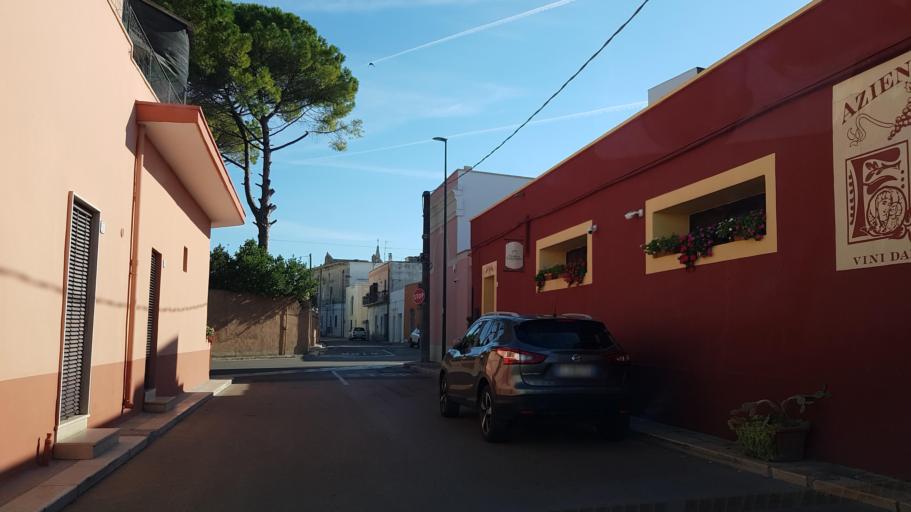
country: IT
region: Apulia
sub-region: Provincia di Lecce
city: Guagnano
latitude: 40.4041
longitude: 17.9507
